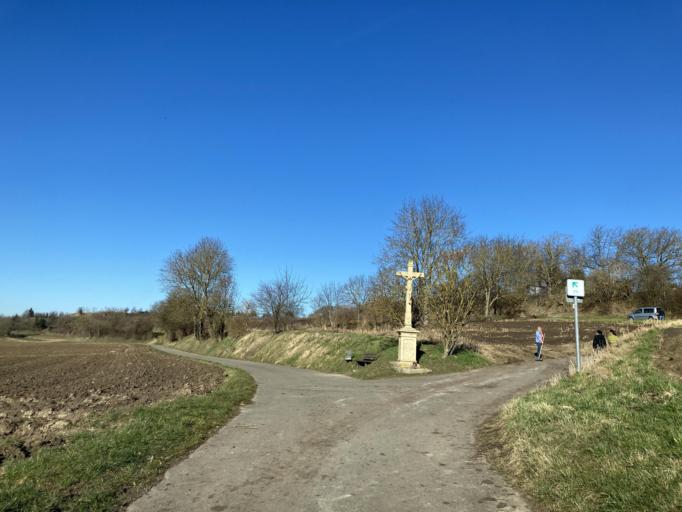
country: DE
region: Baden-Wuerttemberg
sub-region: Freiburg Region
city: Eichstetten
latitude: 48.0766
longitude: 7.7755
